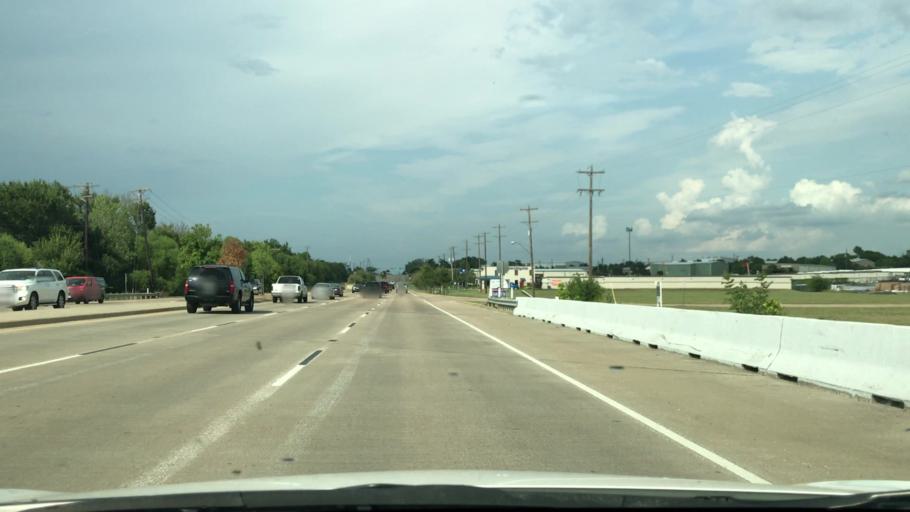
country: US
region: Texas
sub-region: Collin County
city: Wylie
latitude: 32.9983
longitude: -96.5607
